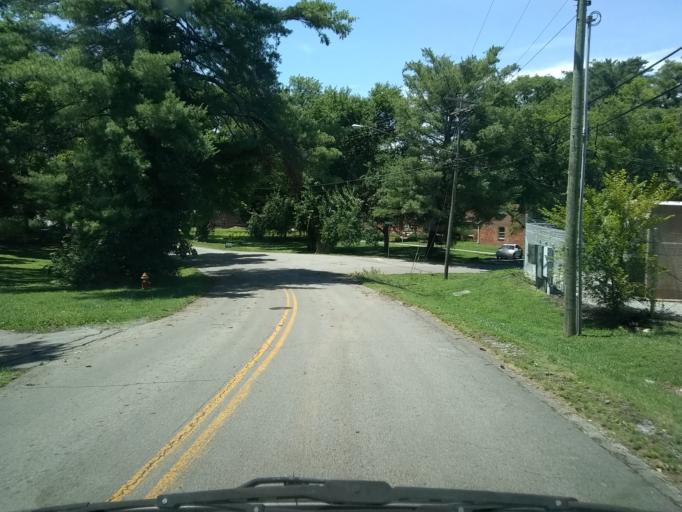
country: US
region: Tennessee
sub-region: Davidson County
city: Oak Hill
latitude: 36.1245
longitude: -86.7107
